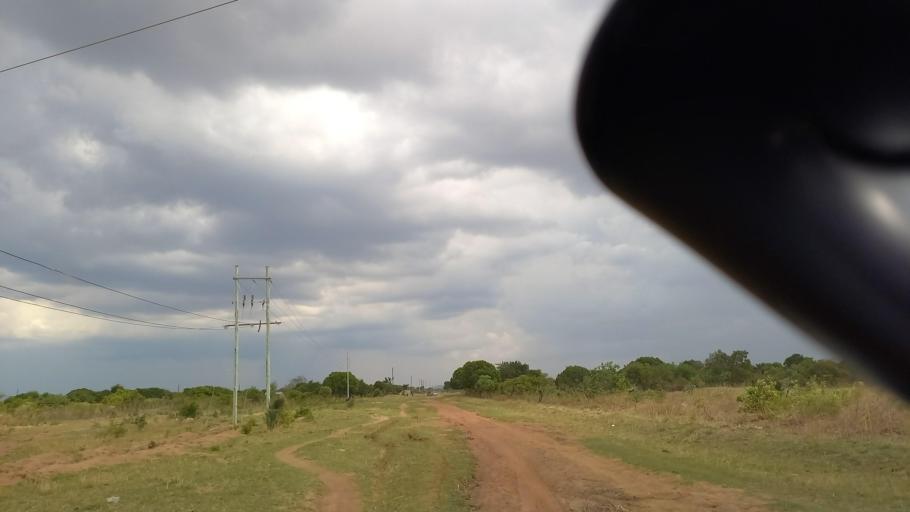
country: ZM
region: Lusaka
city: Kafue
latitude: -15.8479
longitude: 28.1043
